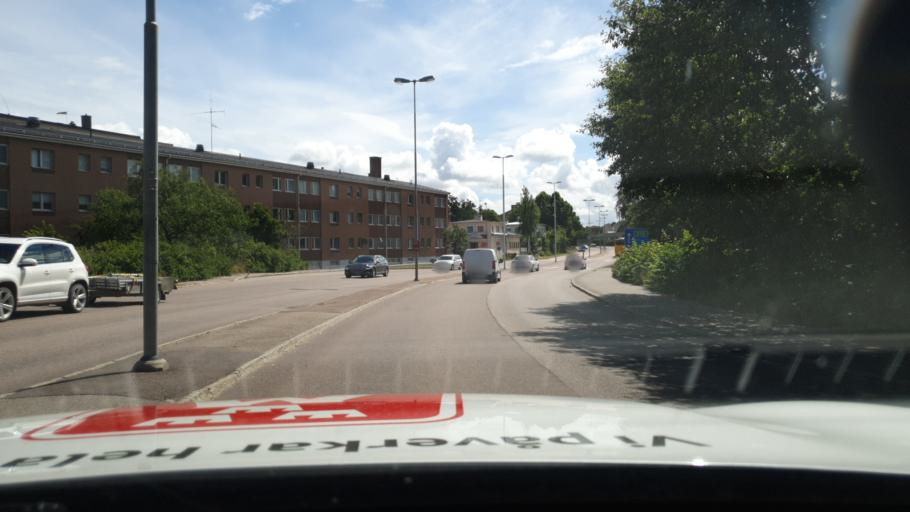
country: SE
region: Vaermland
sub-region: Kristinehamns Kommun
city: Kristinehamn
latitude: 59.3074
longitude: 14.1021
